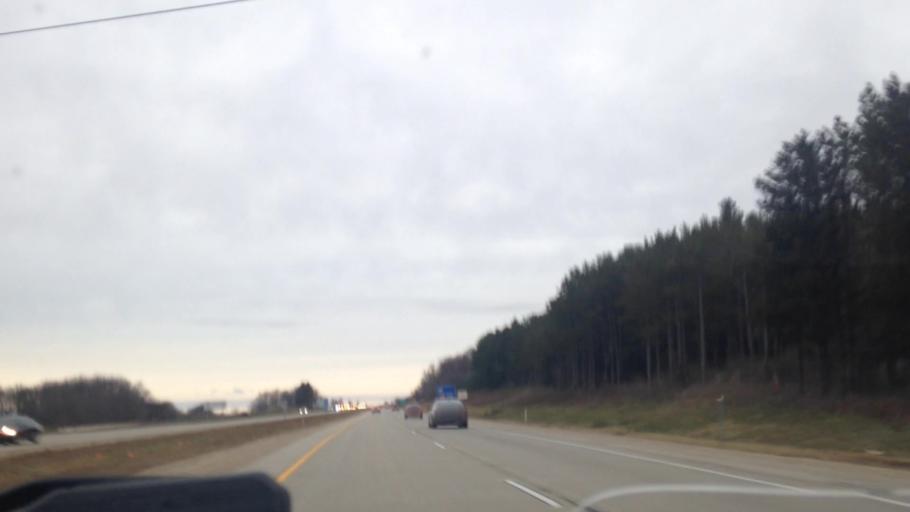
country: US
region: Wisconsin
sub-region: Washington County
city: Slinger
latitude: 43.3577
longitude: -88.2892
